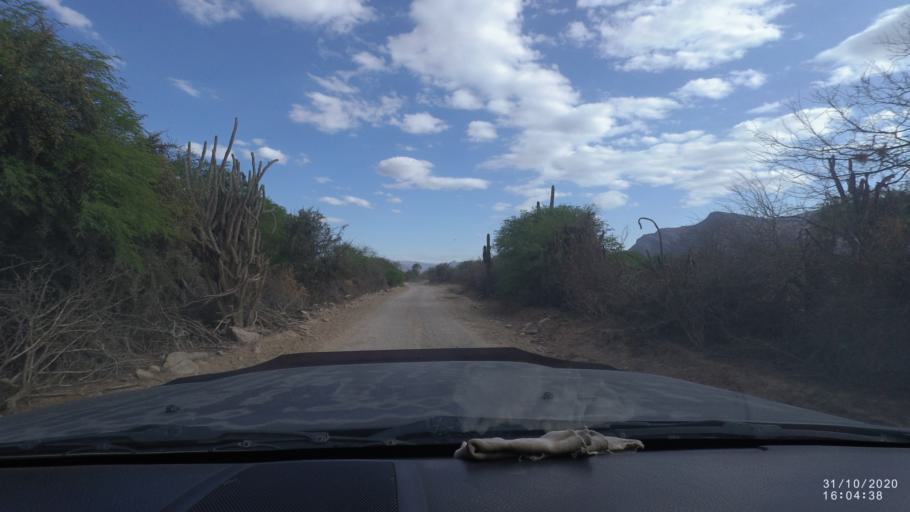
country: BO
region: Chuquisaca
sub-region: Provincia Zudanez
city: Mojocoya
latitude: -18.3607
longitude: -64.6510
